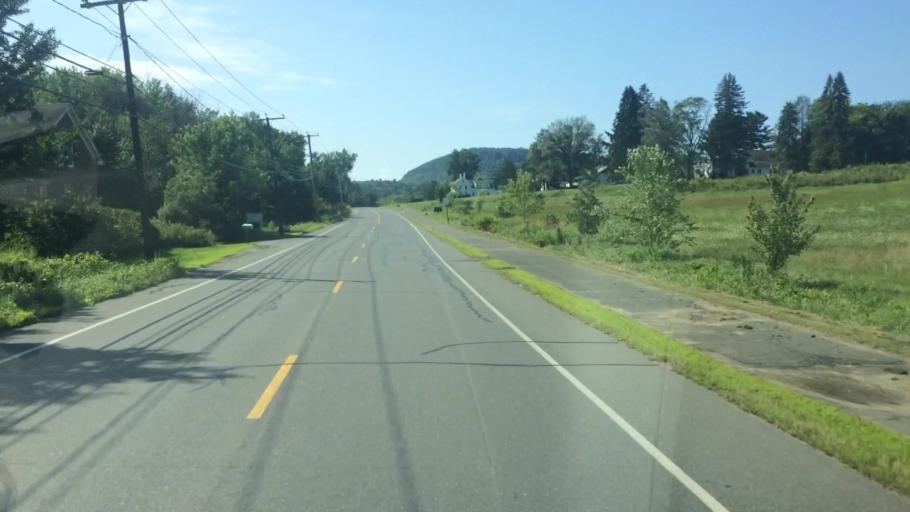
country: US
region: Massachusetts
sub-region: Hampshire County
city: South Amherst
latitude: 42.3291
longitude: -72.5242
